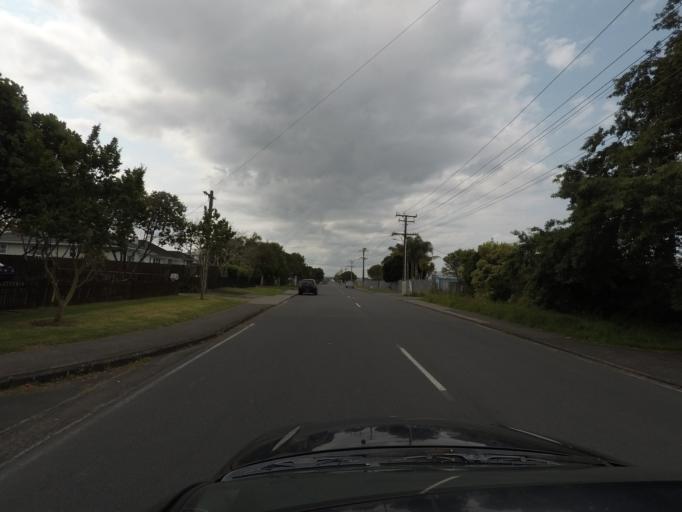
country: NZ
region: Auckland
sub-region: Auckland
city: Rosebank
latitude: -36.8308
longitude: 174.6467
